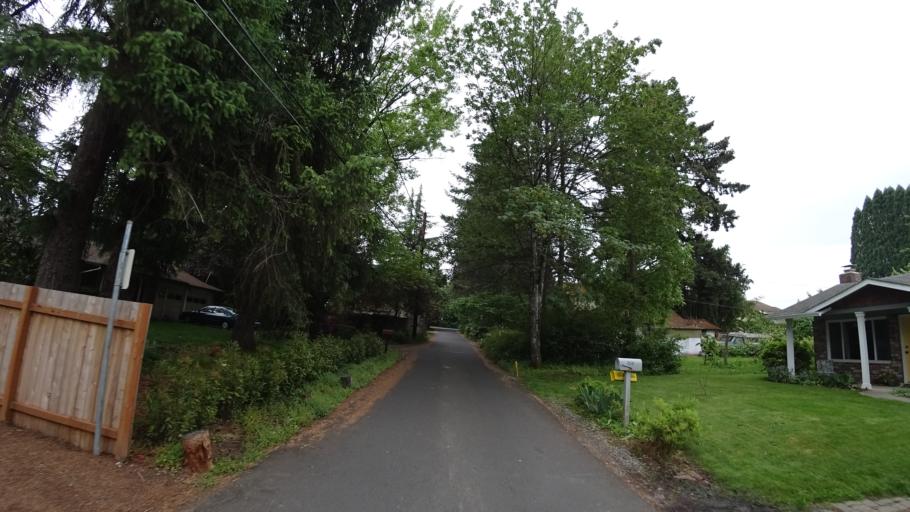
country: US
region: Oregon
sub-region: Washington County
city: Garden Home-Whitford
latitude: 45.4660
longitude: -122.7395
